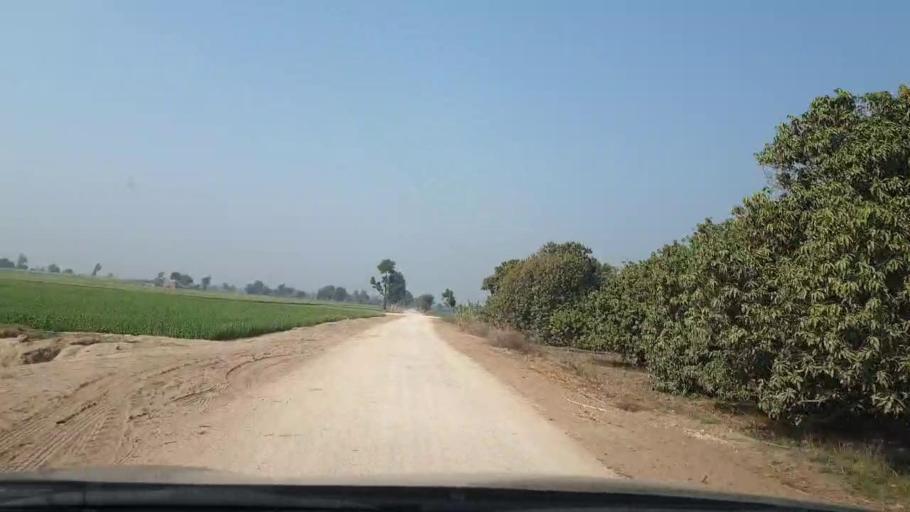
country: PK
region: Sindh
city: Tando Allahyar
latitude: 25.5179
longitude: 68.7473
